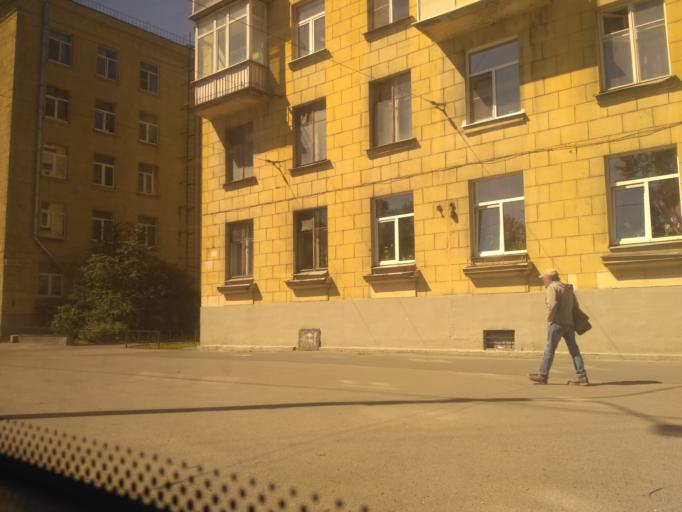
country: RU
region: Leningrad
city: Kalininskiy
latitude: 59.9590
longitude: 30.4222
